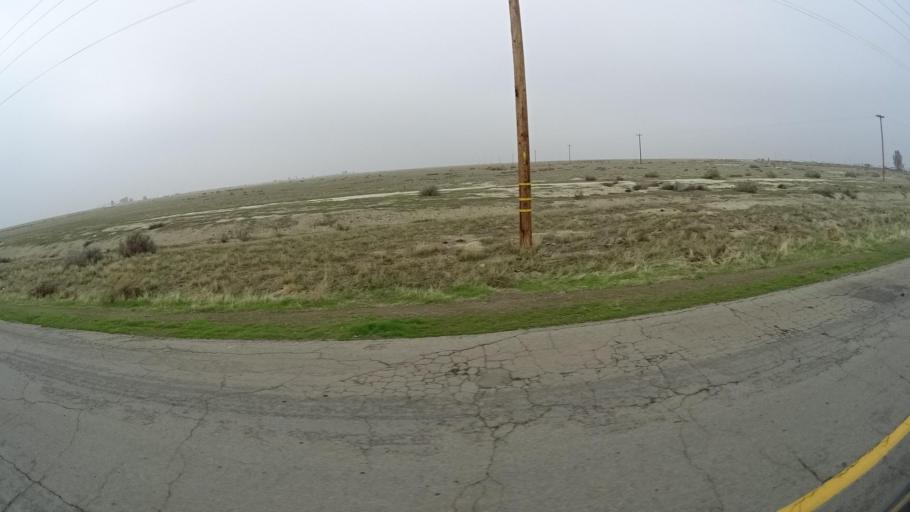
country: US
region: California
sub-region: Tulare County
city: Alpaugh
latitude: 35.7174
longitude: -119.4676
